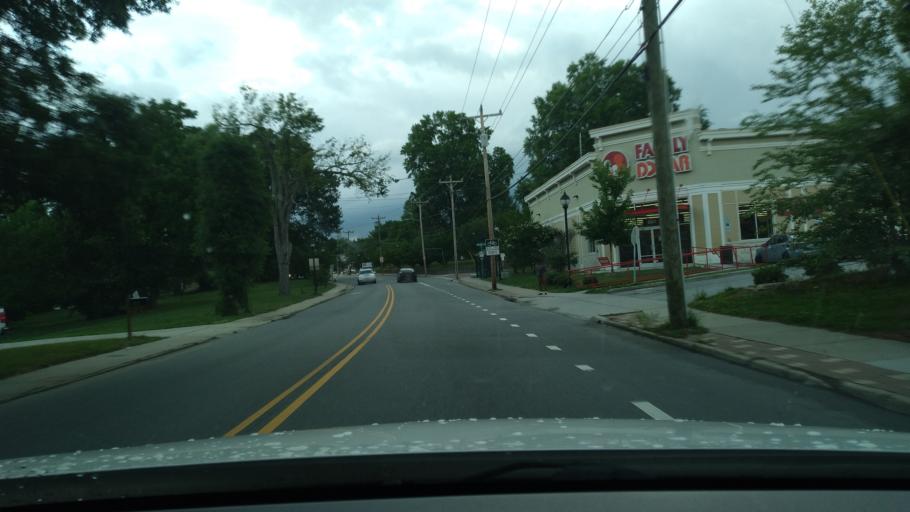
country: US
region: North Carolina
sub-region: Guilford County
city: Greensboro
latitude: 36.0617
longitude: -79.7854
